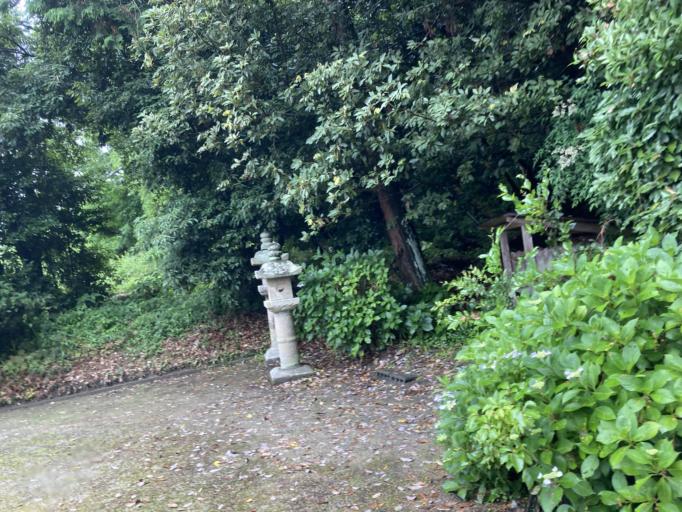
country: JP
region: Nara
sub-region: Ikoma-shi
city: Ikoma
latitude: 34.6239
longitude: 135.7113
